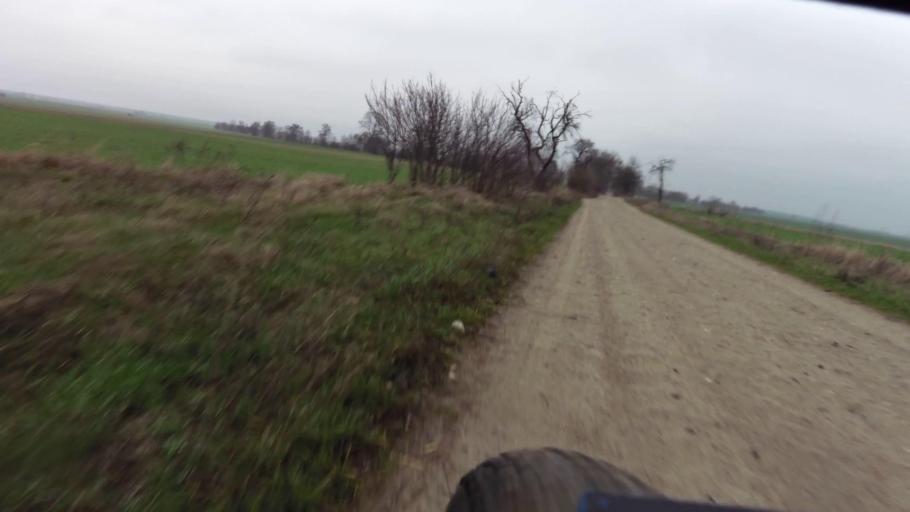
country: PL
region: West Pomeranian Voivodeship
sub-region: Powiat mysliborski
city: Debno
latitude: 52.6592
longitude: 14.7275
